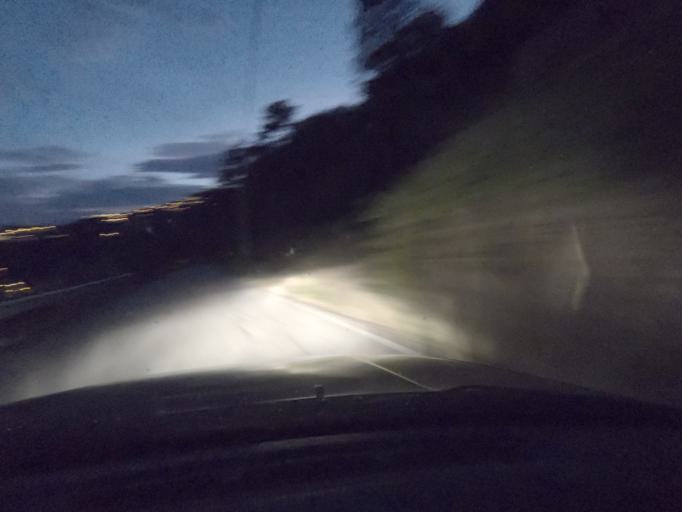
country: PT
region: Vila Real
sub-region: Mesao Frio
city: Mesao Frio
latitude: 41.1903
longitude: -7.8431
